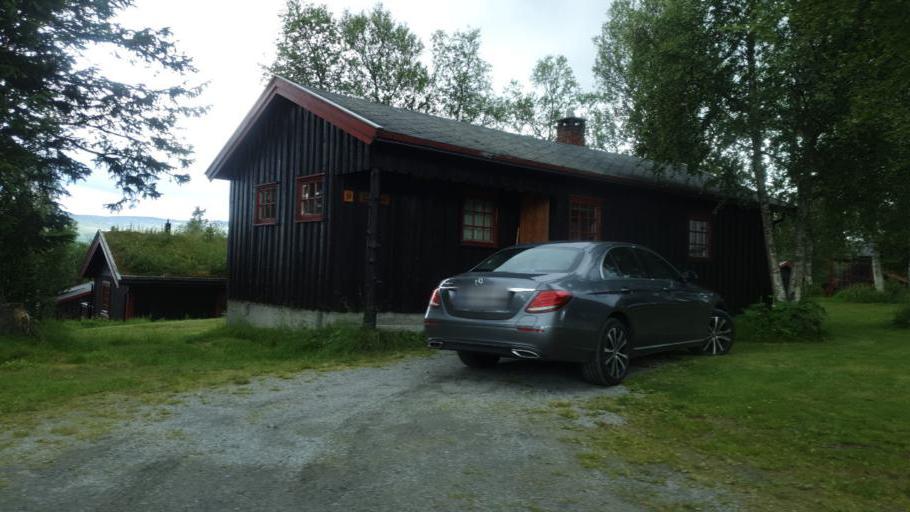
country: NO
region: Oppland
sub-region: Vestre Slidre
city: Slidre
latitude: 61.2432
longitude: 8.9173
